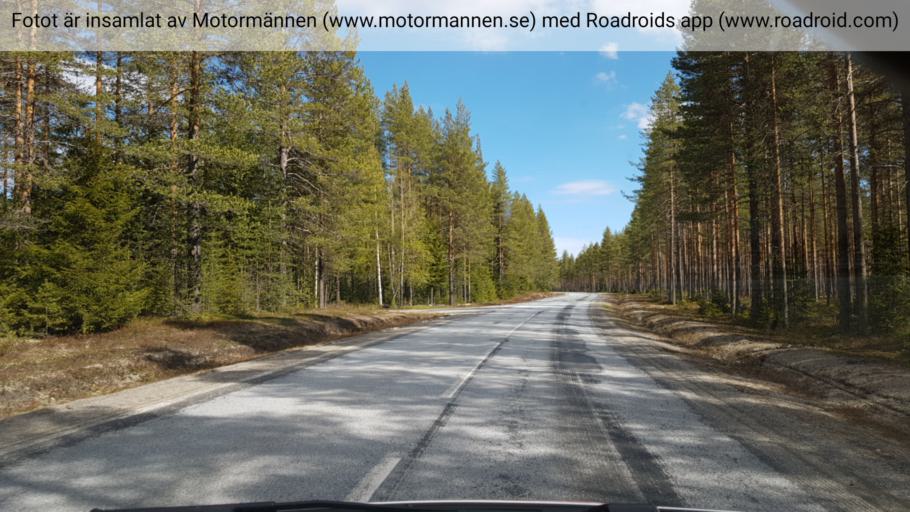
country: SE
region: Vaesterbotten
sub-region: Vindelns Kommun
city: Vindeln
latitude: 64.1665
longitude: 19.7941
